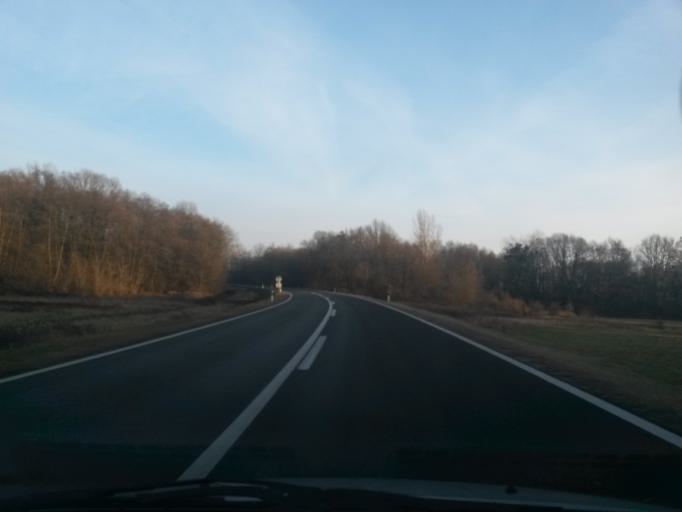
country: HR
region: Varazdinska
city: Jalzabet
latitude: 46.2819
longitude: 16.4874
